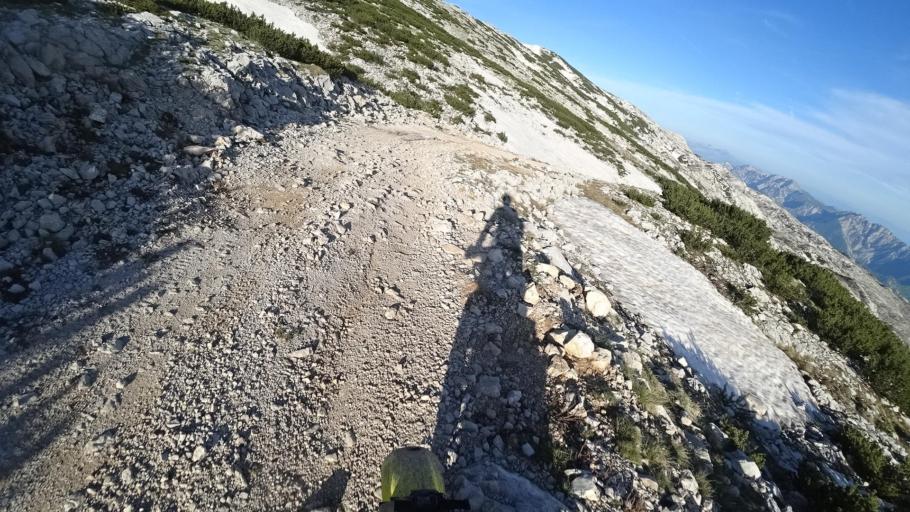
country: BA
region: Federation of Bosnia and Herzegovina
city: Kocerin
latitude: 43.5951
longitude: 17.5434
